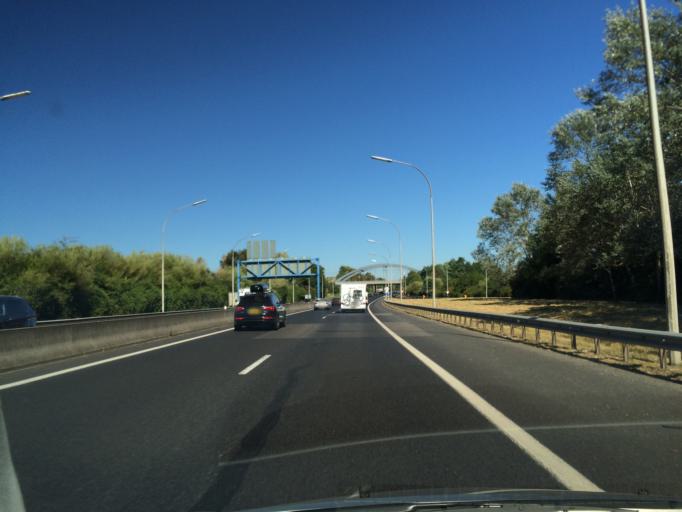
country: LU
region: Luxembourg
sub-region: Canton d'Esch-sur-Alzette
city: Leudelange
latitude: 49.5877
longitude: 6.0854
